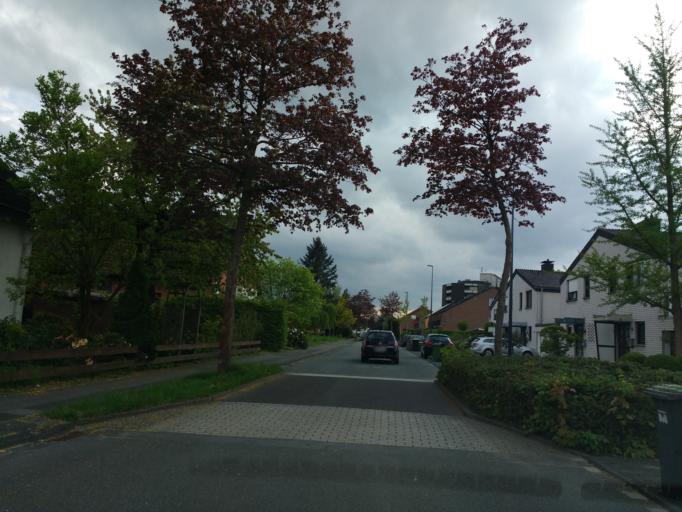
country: DE
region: North Rhine-Westphalia
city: Bad Lippspringe
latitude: 51.7944
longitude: 8.8331
